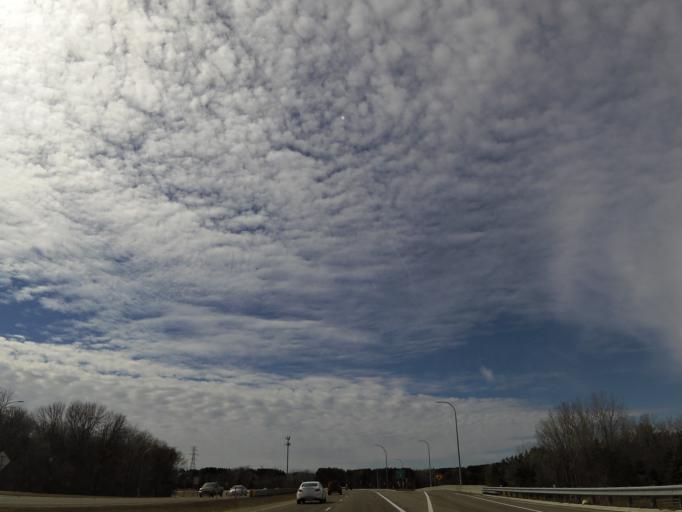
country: US
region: Minnesota
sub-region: Washington County
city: Mahtomedi
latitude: 45.0361
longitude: -92.9461
